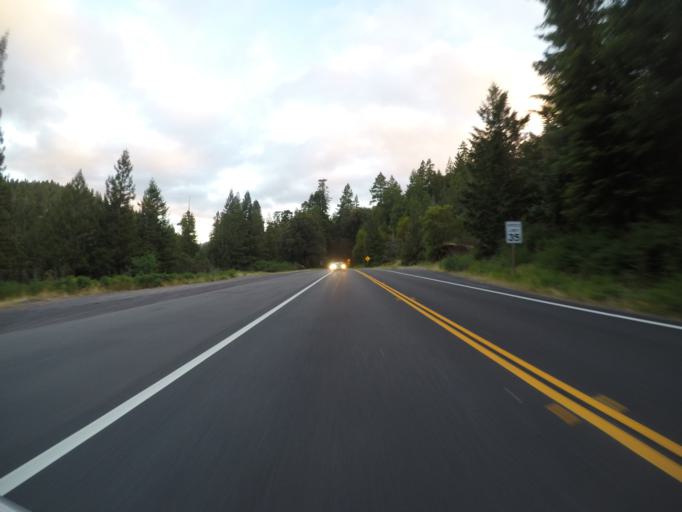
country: US
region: California
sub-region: Humboldt County
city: Redway
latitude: 40.0304
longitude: -123.7938
